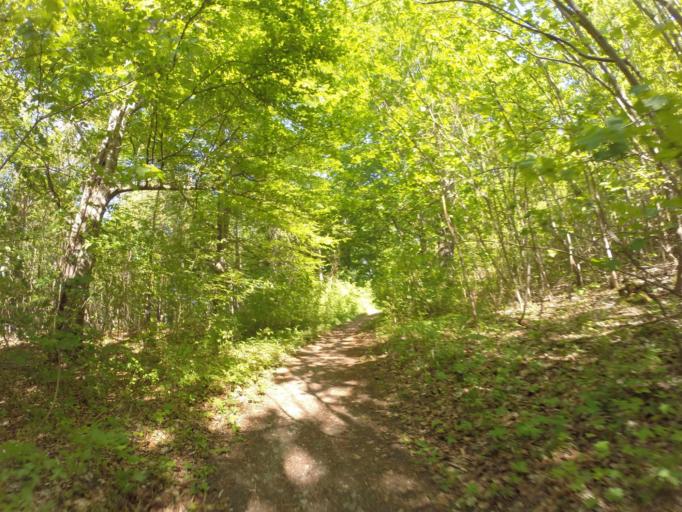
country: DE
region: Thuringia
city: Golmsdorf
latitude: 50.9452
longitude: 11.6480
